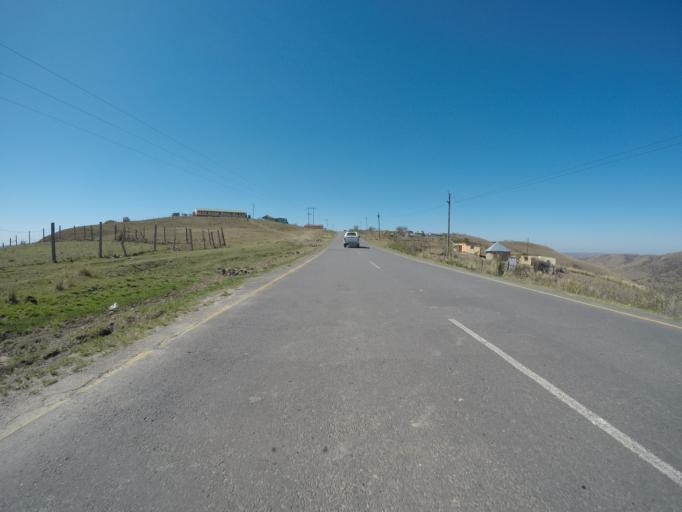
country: ZA
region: Eastern Cape
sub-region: OR Tambo District Municipality
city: Mthatha
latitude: -31.9036
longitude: 28.9470
